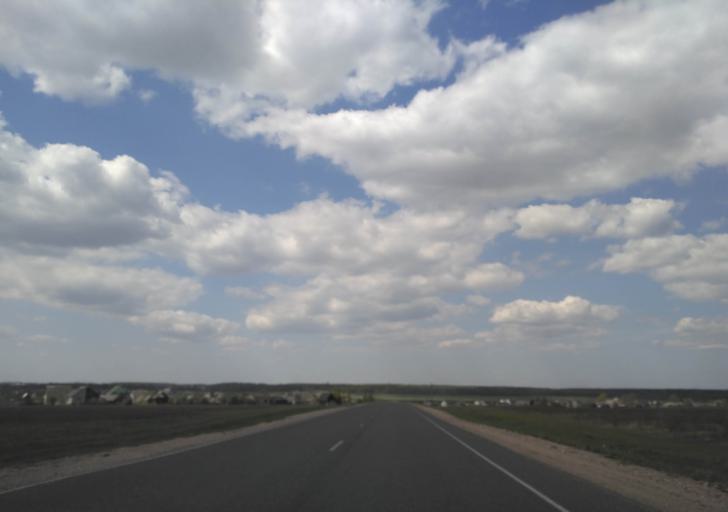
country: BY
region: Minsk
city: Vilyeyka
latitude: 54.5155
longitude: 26.9853
